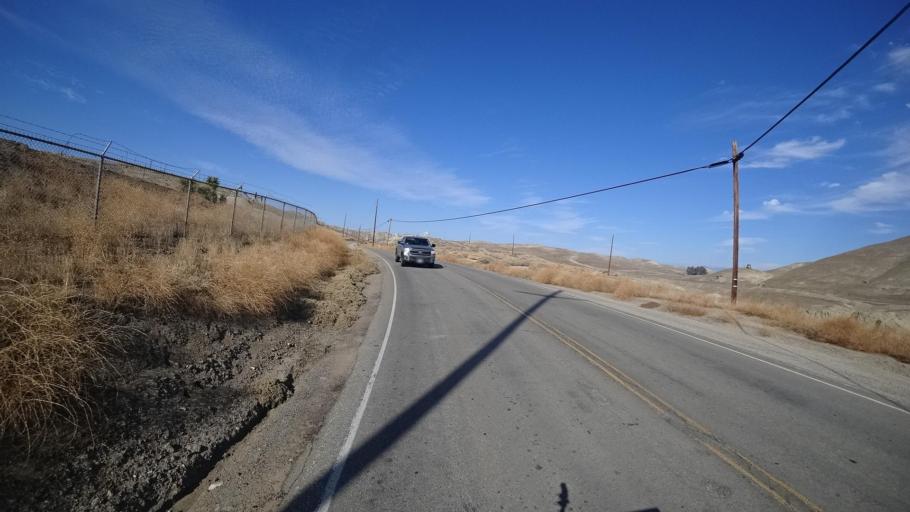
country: US
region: California
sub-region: Kern County
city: Oildale
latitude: 35.5630
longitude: -118.9552
